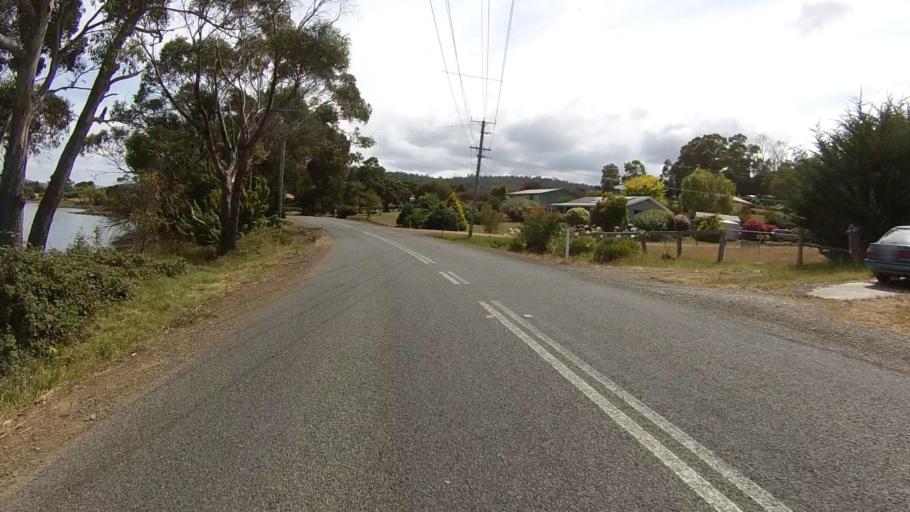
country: AU
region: Tasmania
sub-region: Huon Valley
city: Cygnet
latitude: -43.1925
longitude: 147.1023
